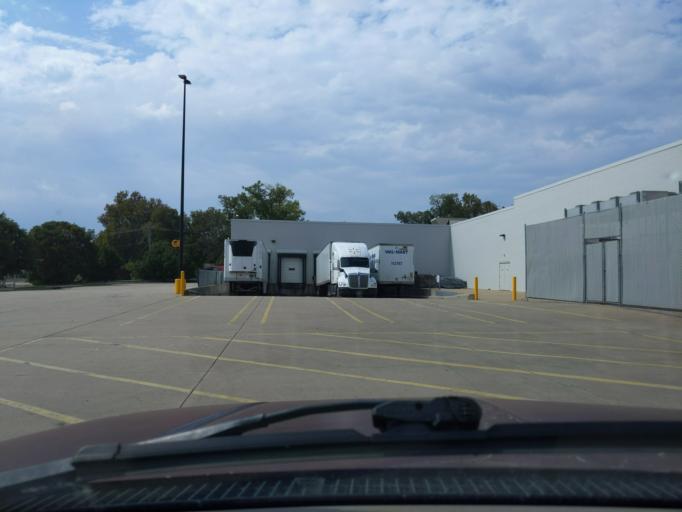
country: US
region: Oklahoma
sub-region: Tulsa County
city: Sand Springs
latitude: 36.1341
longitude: -96.1203
